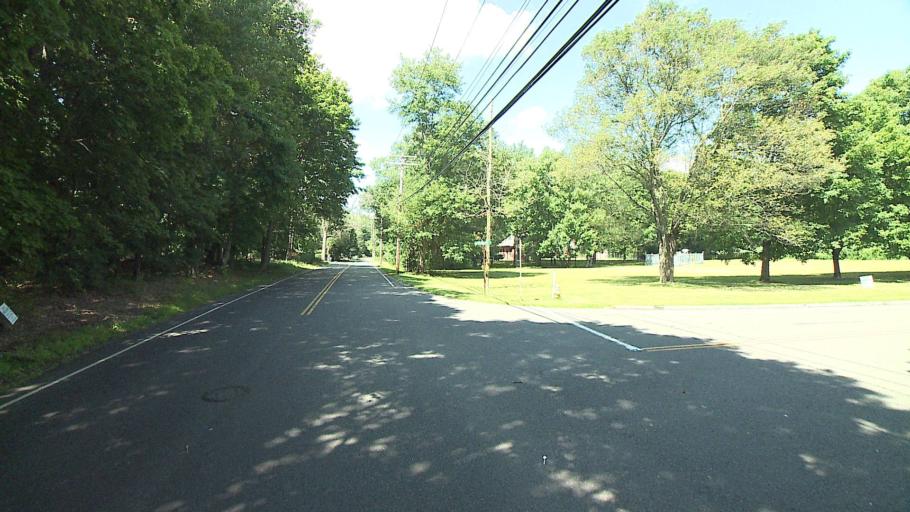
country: US
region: Connecticut
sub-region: Fairfield County
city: Trumbull
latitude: 41.2547
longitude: -73.1646
